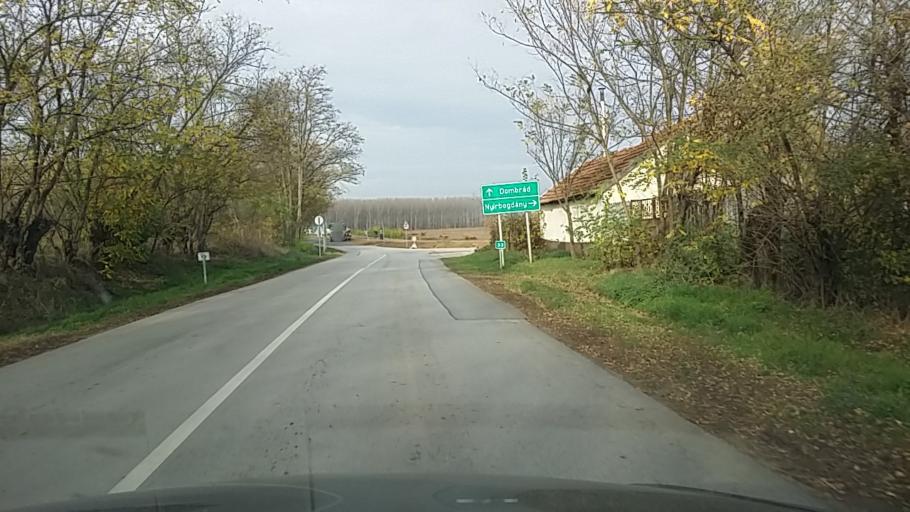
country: HU
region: Szabolcs-Szatmar-Bereg
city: Nyirbogdany
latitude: 48.0636
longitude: 21.8600
